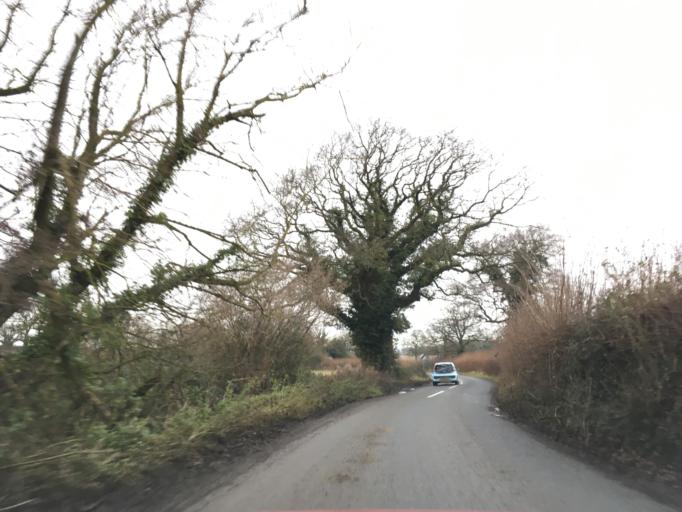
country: GB
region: England
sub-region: Gloucestershire
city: Wotton-under-Edge
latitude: 51.6073
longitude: -2.3405
